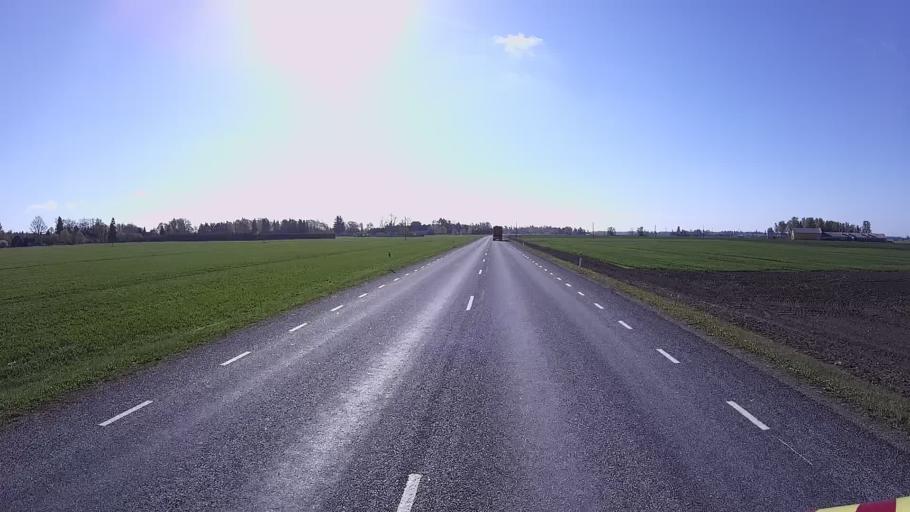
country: EE
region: Jaervamaa
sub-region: Tueri vald
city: Sarevere
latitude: 58.7645
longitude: 25.5402
